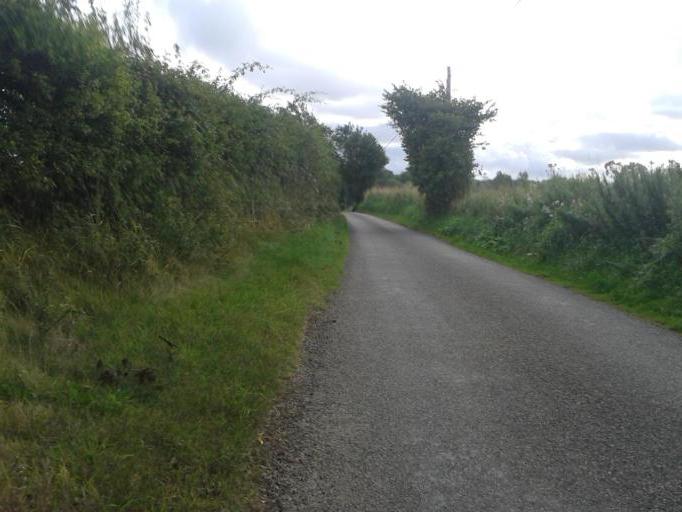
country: GB
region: England
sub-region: Hertfordshire
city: Buntingford
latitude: 51.9782
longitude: 0.0915
